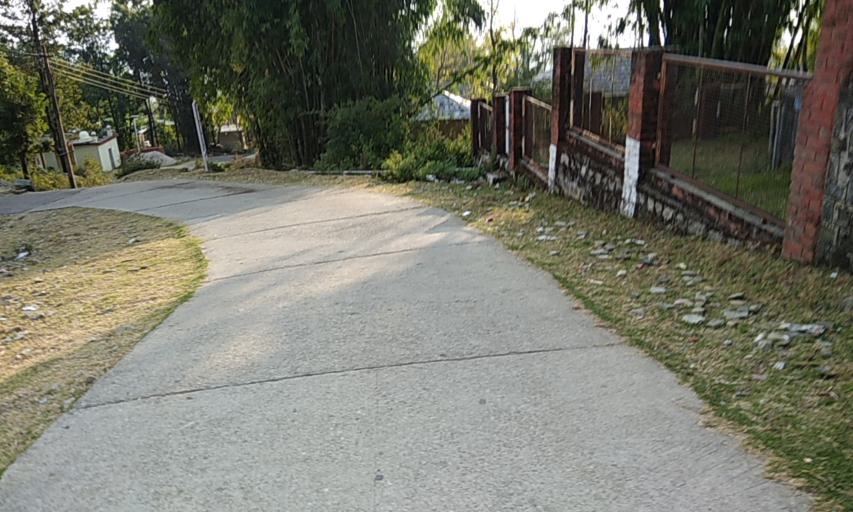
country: IN
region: Himachal Pradesh
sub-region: Kangra
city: Palampur
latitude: 32.1195
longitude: 76.5851
